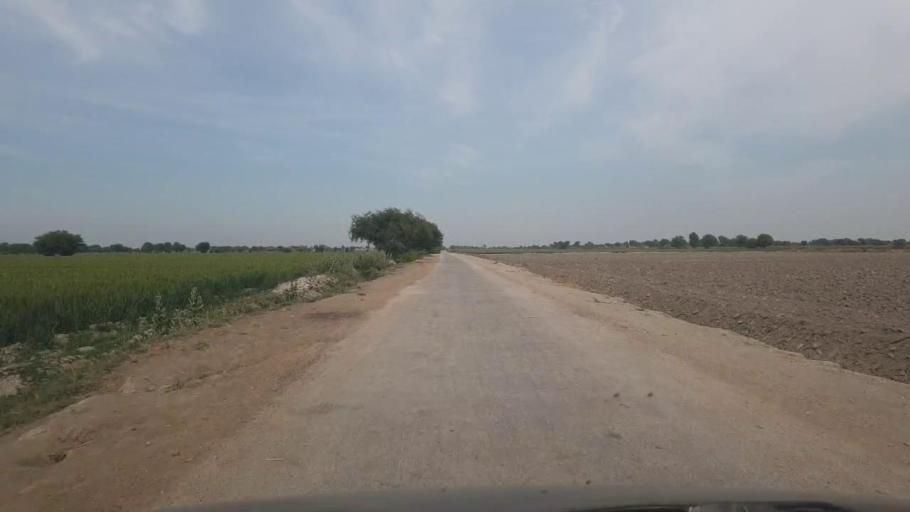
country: PK
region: Sindh
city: Kunri
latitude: 25.2464
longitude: 69.6198
